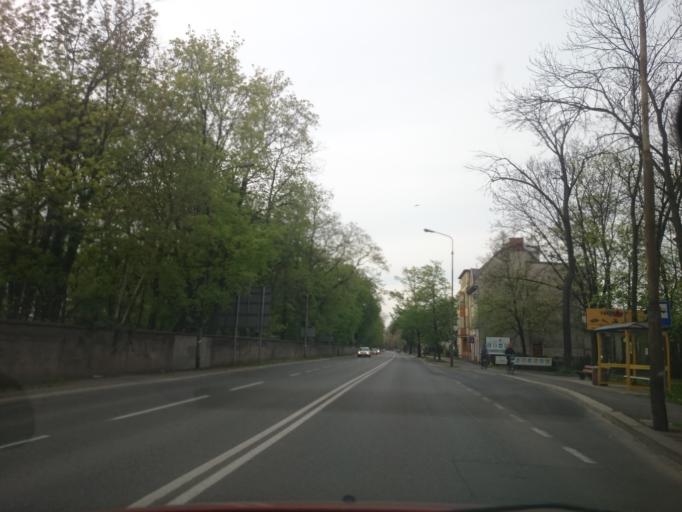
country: PL
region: Opole Voivodeship
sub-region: Powiat opolski
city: Opole
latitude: 50.6722
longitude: 17.9111
